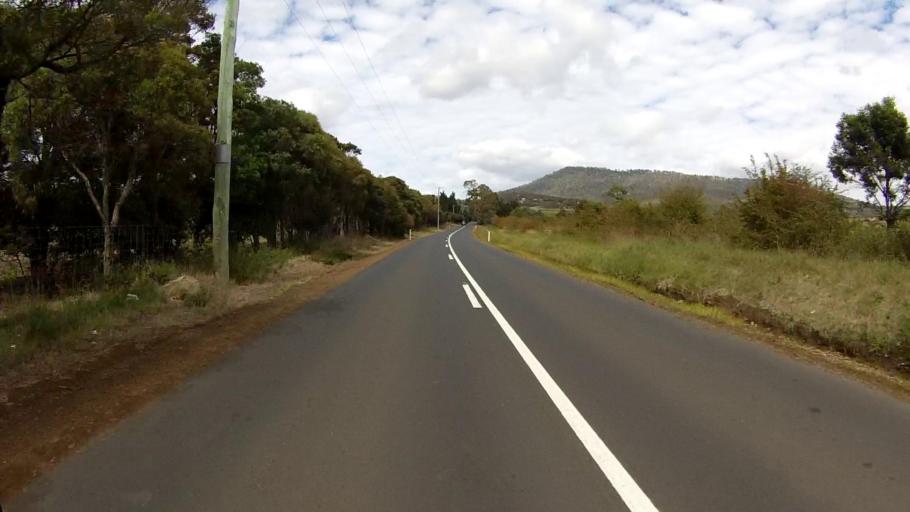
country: AU
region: Tasmania
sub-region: Clarence
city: Cambridge
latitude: -42.7593
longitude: 147.4019
